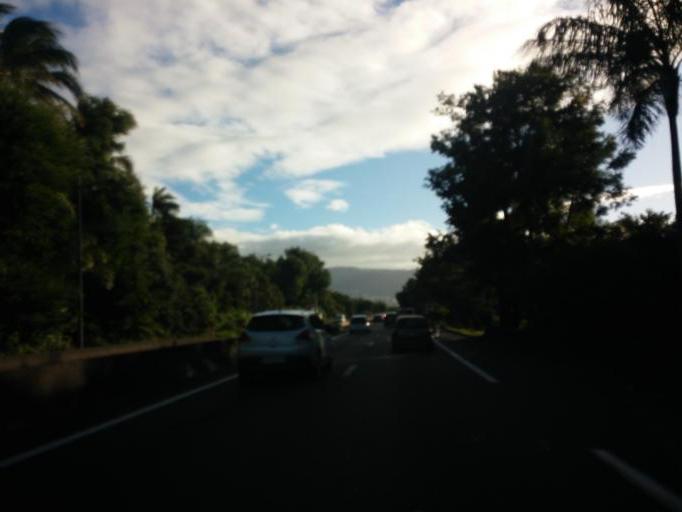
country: RE
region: Reunion
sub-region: Reunion
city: Saint-Denis
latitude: -20.8863
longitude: 55.4937
